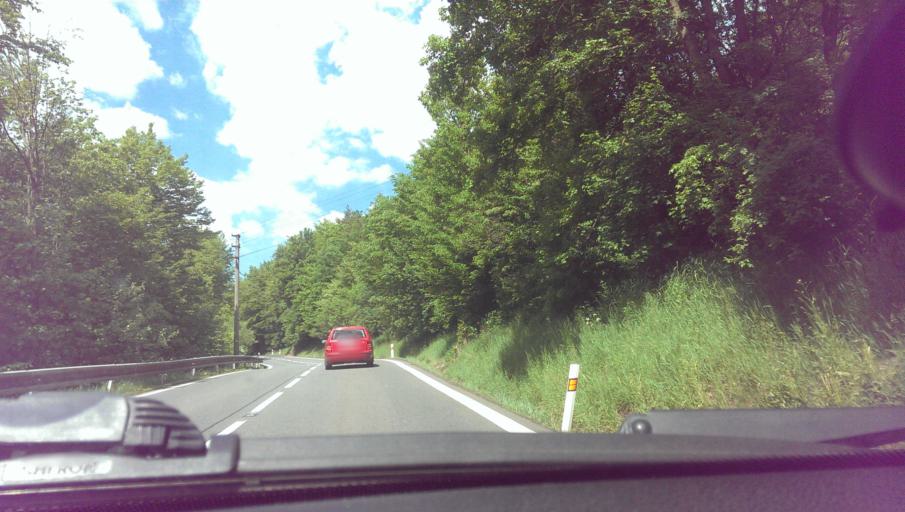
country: CZ
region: Zlin
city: Valasska Polanka
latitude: 49.2442
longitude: 17.9690
